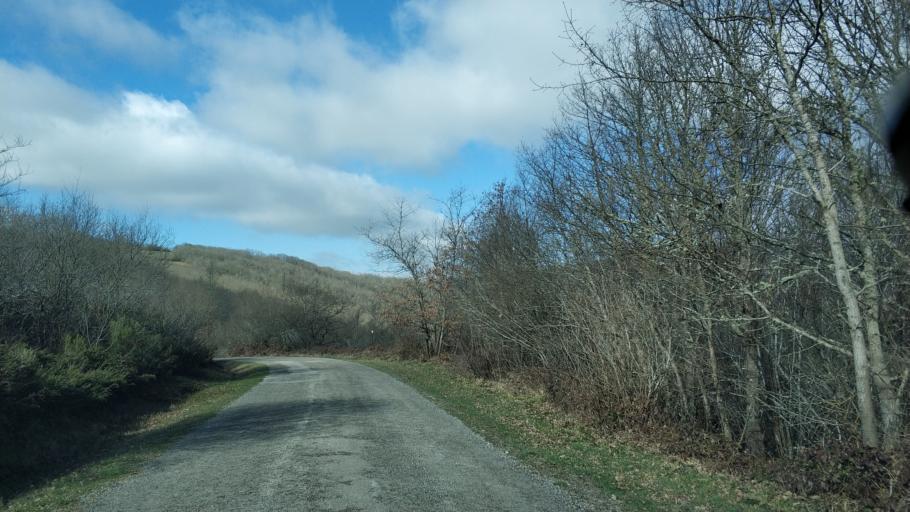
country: ES
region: Castille and Leon
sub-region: Provincia de Burgos
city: Arija
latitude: 42.9022
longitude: -4.0161
